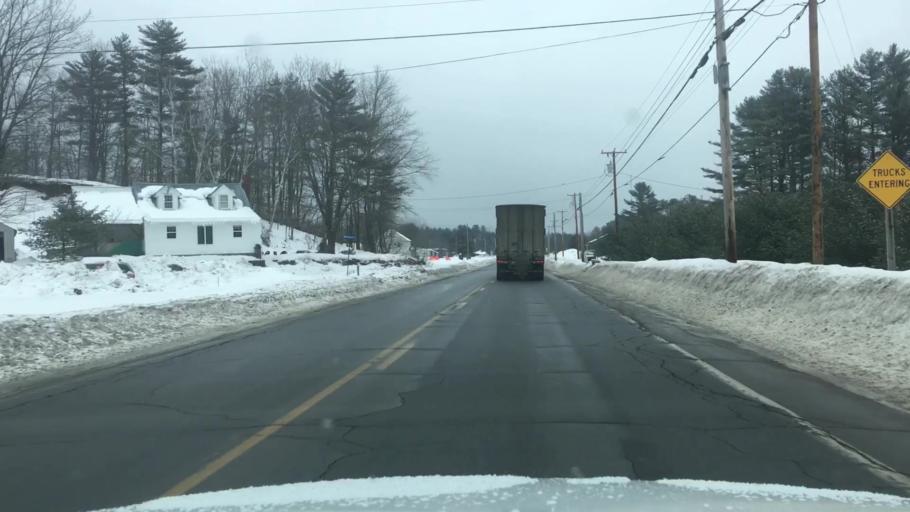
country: US
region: Maine
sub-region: Oxford County
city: Peru
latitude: 44.5185
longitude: -70.4159
